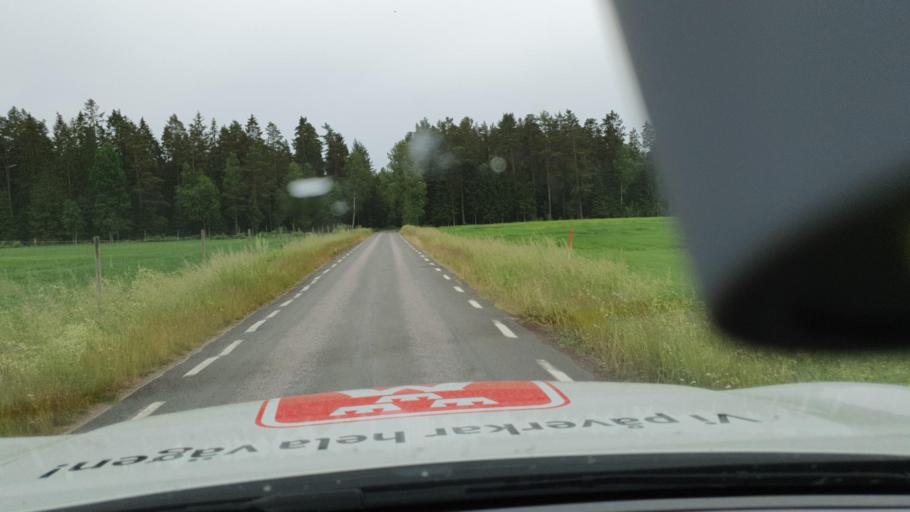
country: SE
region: Vaestra Goetaland
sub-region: Tibro Kommun
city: Tibro
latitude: 58.3358
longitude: 14.1948
